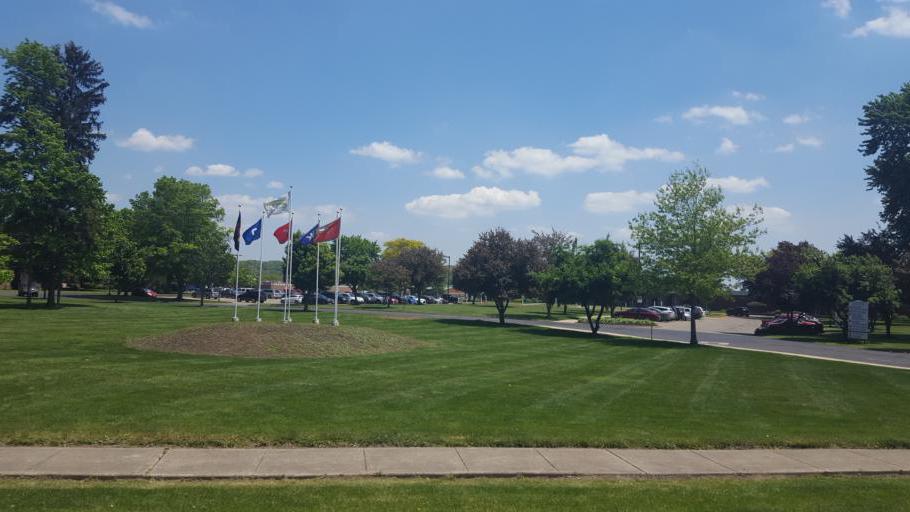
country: US
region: Ohio
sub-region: Knox County
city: Mount Vernon
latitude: 40.3759
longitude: -82.4775
